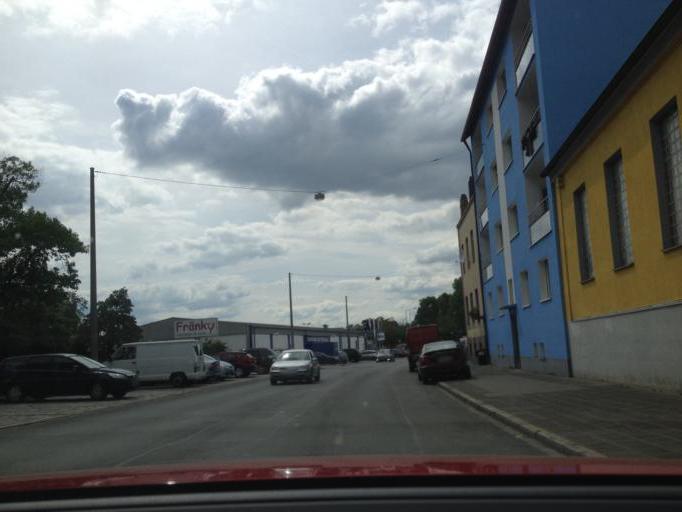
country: DE
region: Bavaria
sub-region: Regierungsbezirk Mittelfranken
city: Grossreuth bei Schweinau
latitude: 49.4352
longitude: 11.0451
